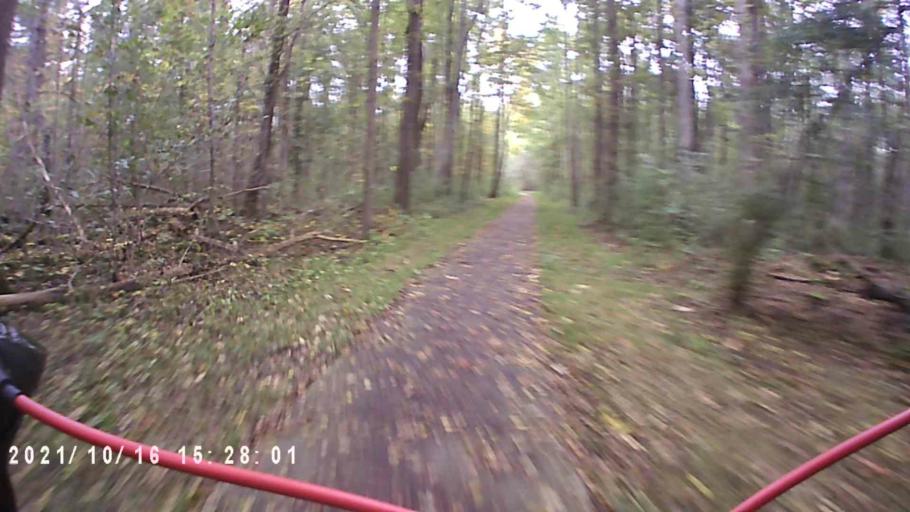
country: NL
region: Friesland
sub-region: Gemeente Dongeradeel
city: Anjum
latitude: 53.4041
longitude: 6.2265
